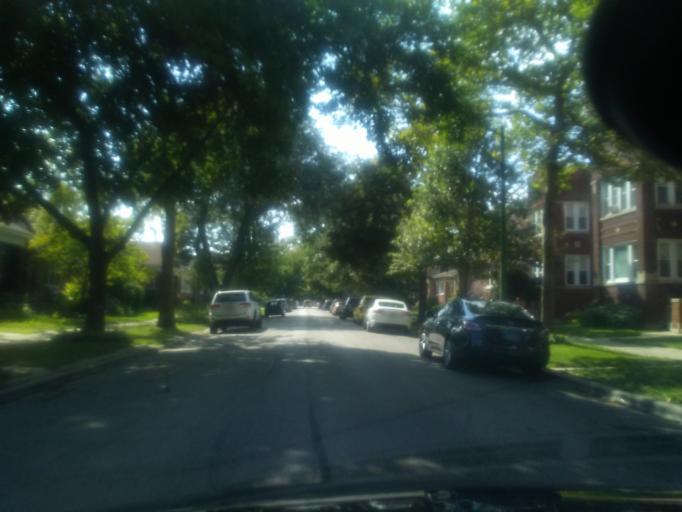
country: US
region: Illinois
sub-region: Cook County
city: Harwood Heights
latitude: 41.9597
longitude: -87.7604
